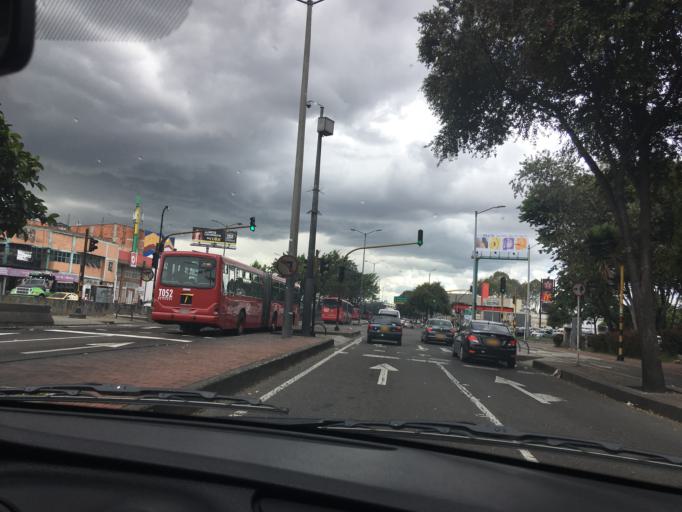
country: CO
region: Bogota D.C.
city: Barrio San Luis
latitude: 4.6687
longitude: -74.0629
